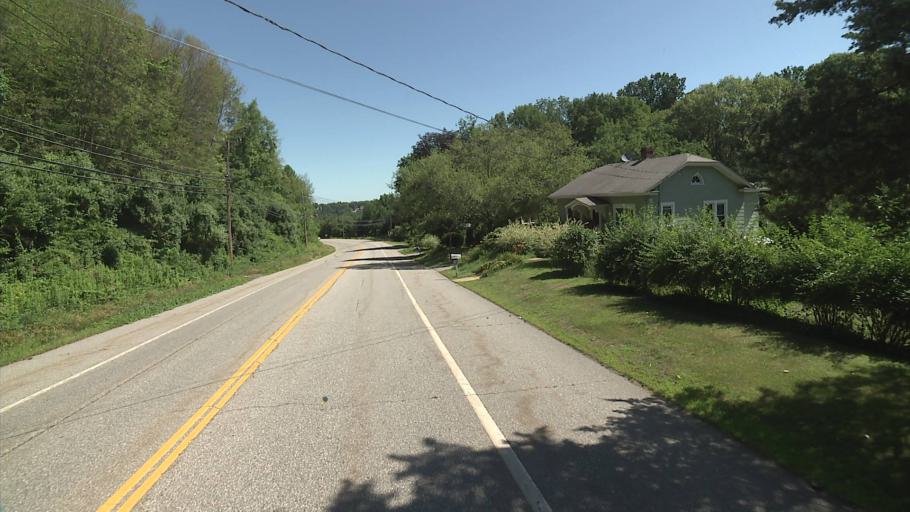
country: US
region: Connecticut
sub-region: Windham County
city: Willimantic
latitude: 41.7034
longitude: -72.2168
